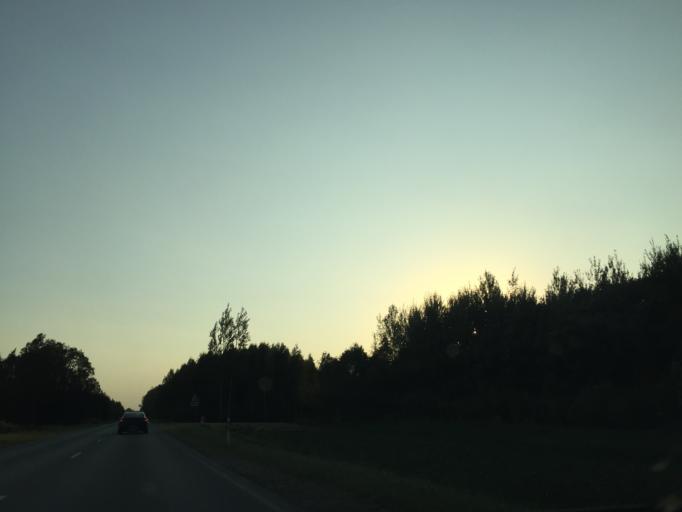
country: LV
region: Lielvarde
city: Lielvarde
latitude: 56.7844
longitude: 24.7954
